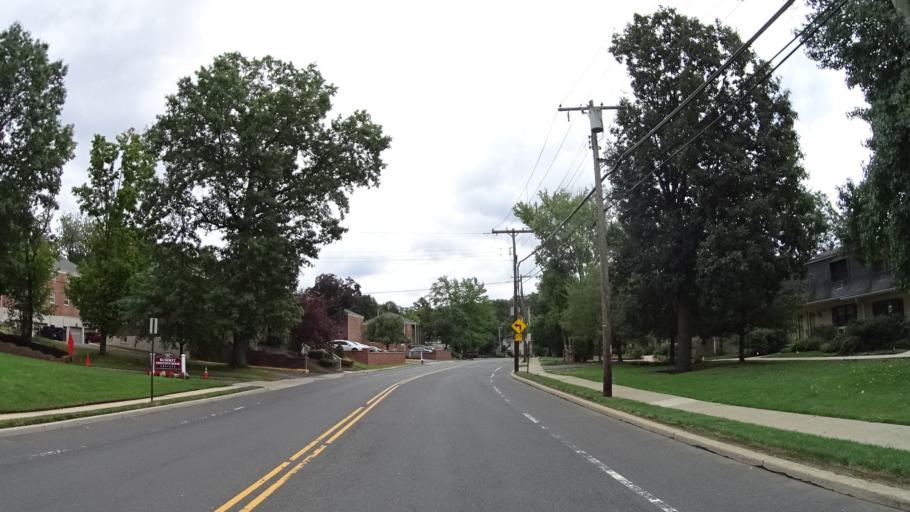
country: US
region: New Jersey
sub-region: Union County
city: New Providence
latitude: 40.7126
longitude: -74.3836
